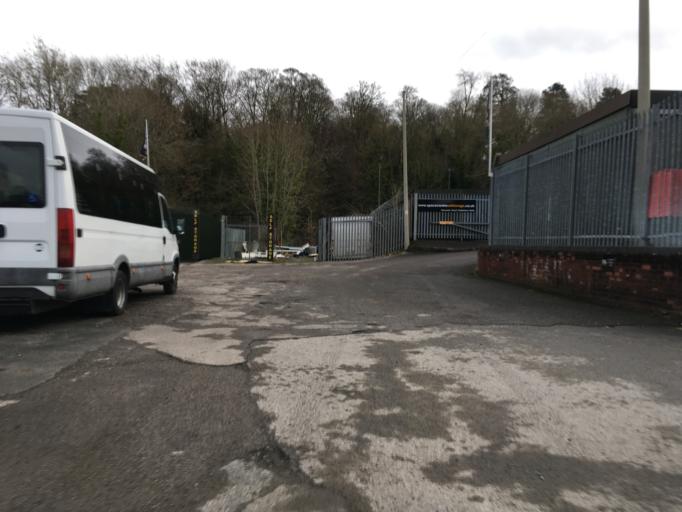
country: GB
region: England
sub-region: Gloucestershire
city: Stroud
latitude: 51.7428
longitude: -2.2322
